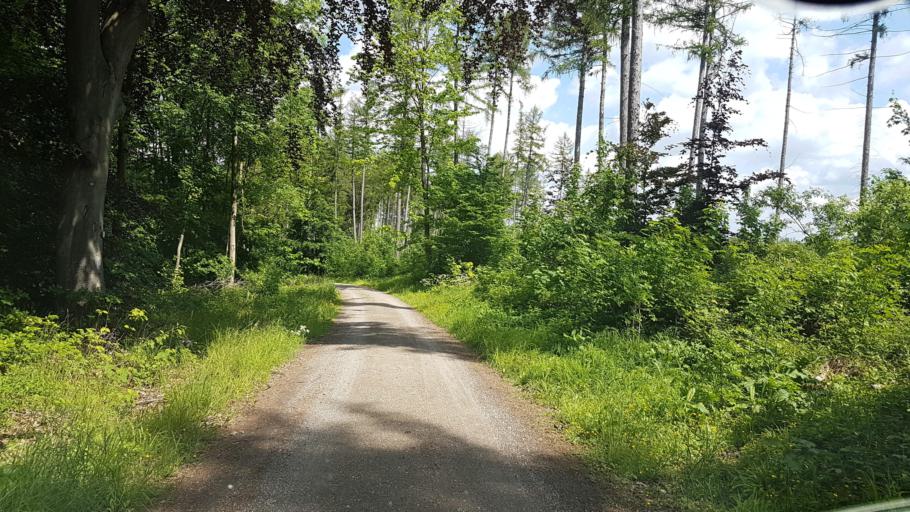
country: DE
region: Lower Saxony
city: Warberg
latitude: 52.1650
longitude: 10.8984
